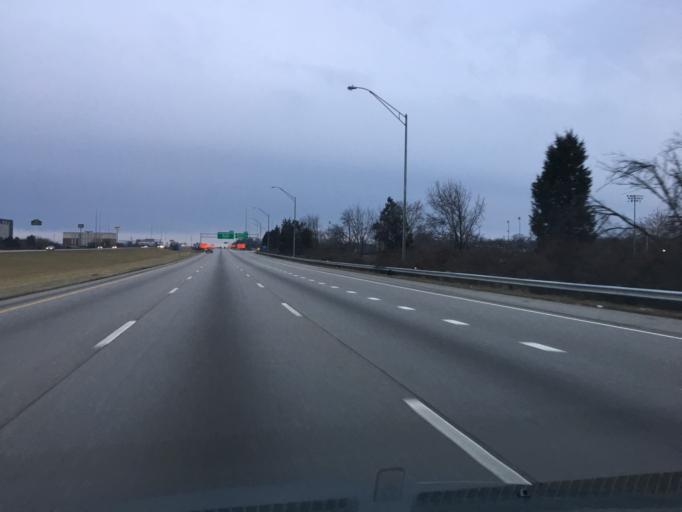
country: US
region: Ohio
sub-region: Hamilton County
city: Glendale
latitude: 39.2759
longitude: -84.4412
